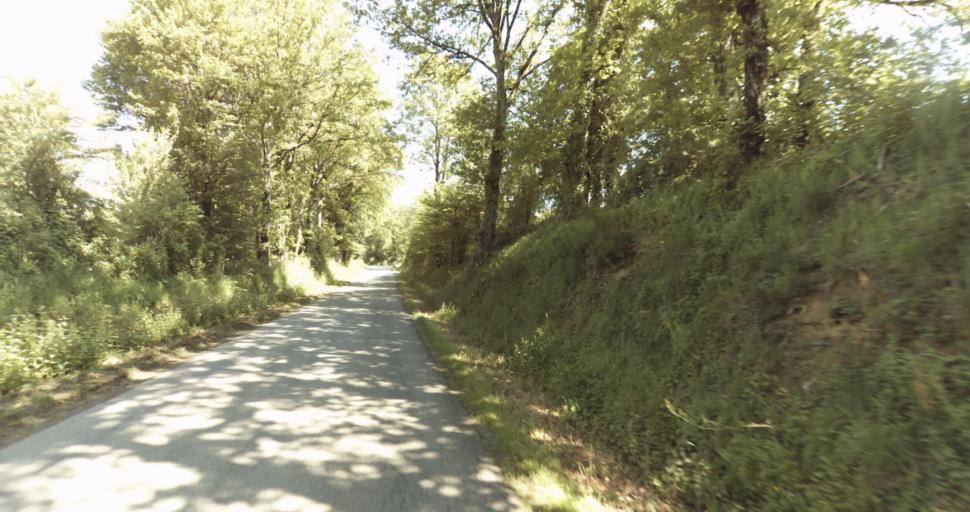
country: FR
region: Limousin
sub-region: Departement de la Haute-Vienne
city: Le Vigen
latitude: 45.7231
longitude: 1.2874
